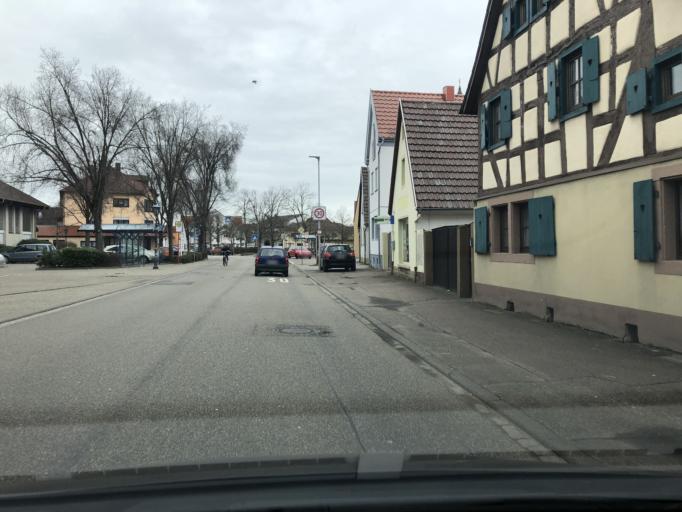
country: DE
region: Baden-Wuerttemberg
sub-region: Karlsruhe Region
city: Ubstadt-Weiher
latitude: 49.1782
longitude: 8.6211
